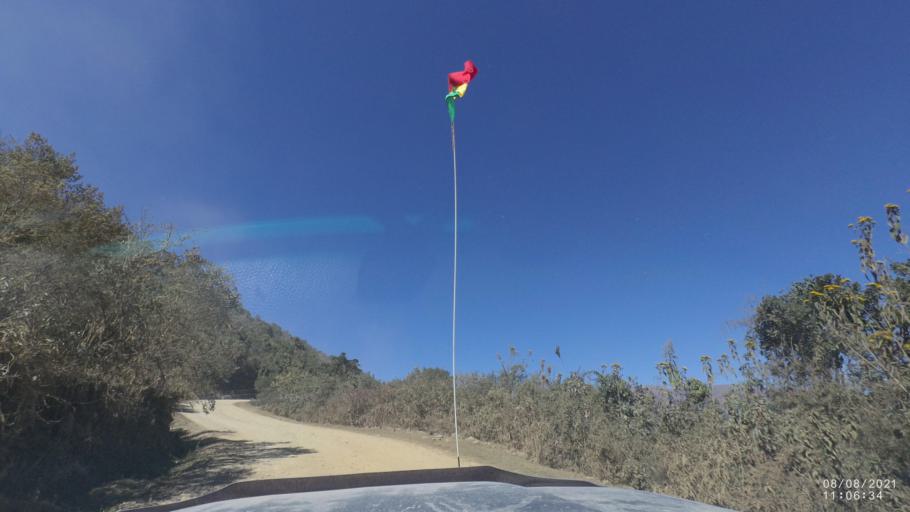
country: BO
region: Cochabamba
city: Colchani
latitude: -16.7636
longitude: -66.6840
